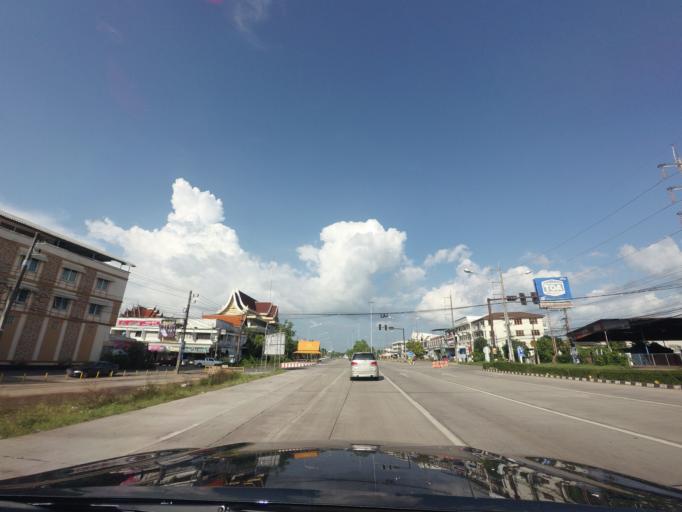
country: TH
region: Nong Khai
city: Nong Khai
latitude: 17.8831
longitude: 102.7566
